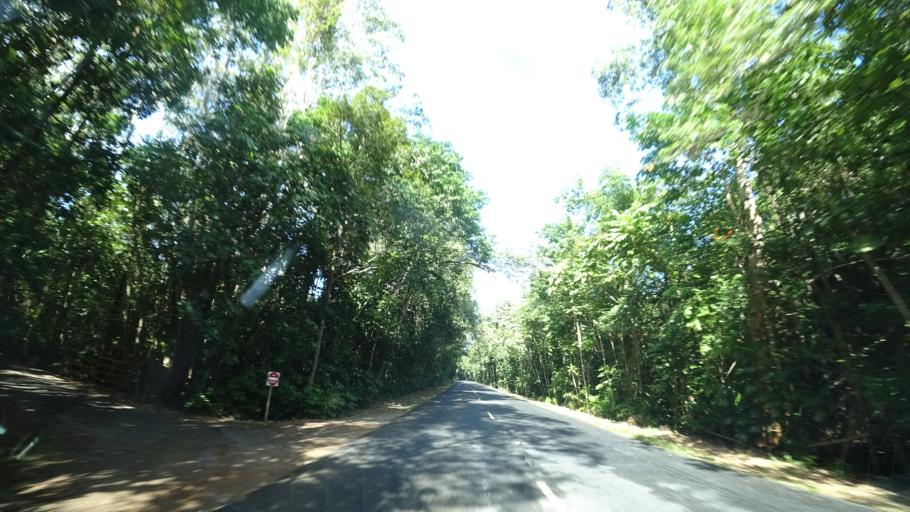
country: AU
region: Queensland
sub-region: Cairns
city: Port Douglas
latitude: -16.1327
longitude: 145.4520
